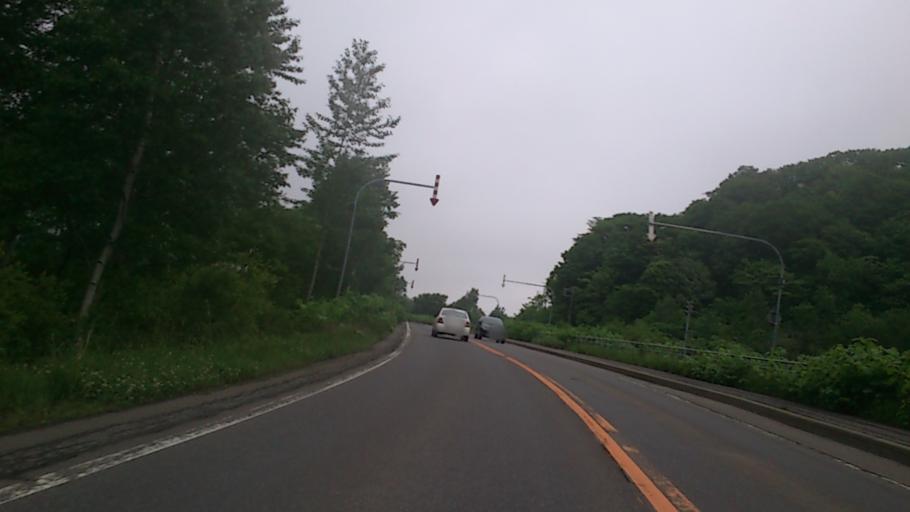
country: JP
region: Hokkaido
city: Niseko Town
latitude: 42.8315
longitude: 140.8932
